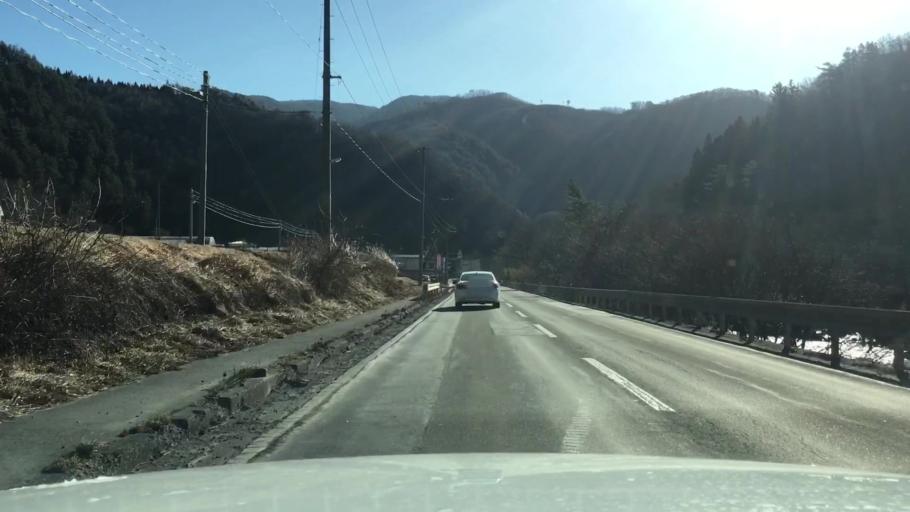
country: JP
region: Iwate
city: Miyako
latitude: 39.5950
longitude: 141.6604
